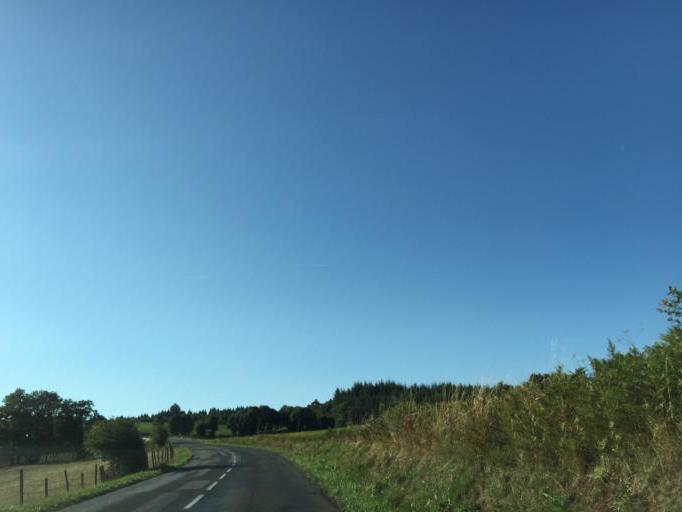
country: FR
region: Midi-Pyrenees
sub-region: Departement de l'Aveyron
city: Salles-Curan
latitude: 44.1329
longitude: 2.8843
